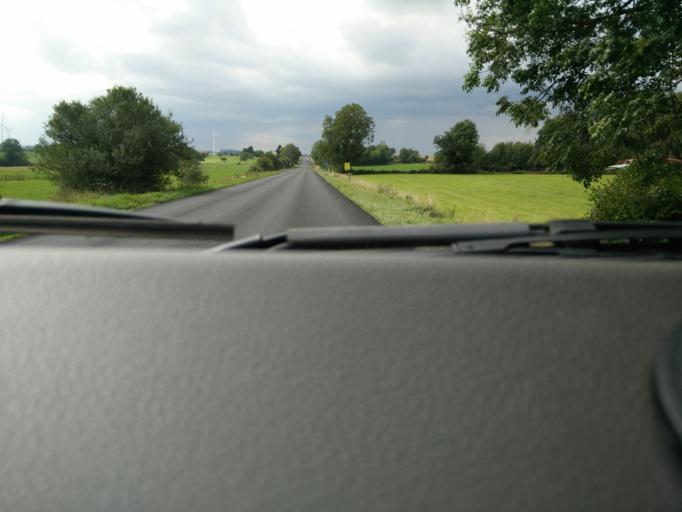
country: FR
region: Champagne-Ardenne
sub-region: Departement des Ardennes
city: Signy-le-Petit
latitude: 49.8710
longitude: 4.3434
